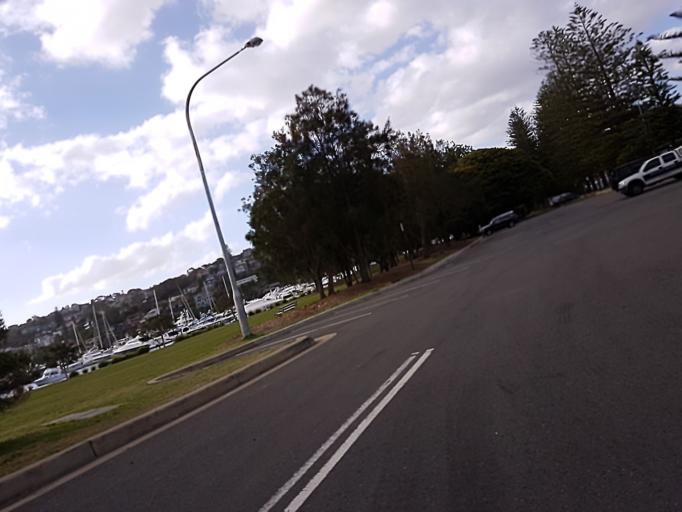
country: AU
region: New South Wales
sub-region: Manly Vale
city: Clontarf
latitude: -33.8067
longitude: 151.2464
